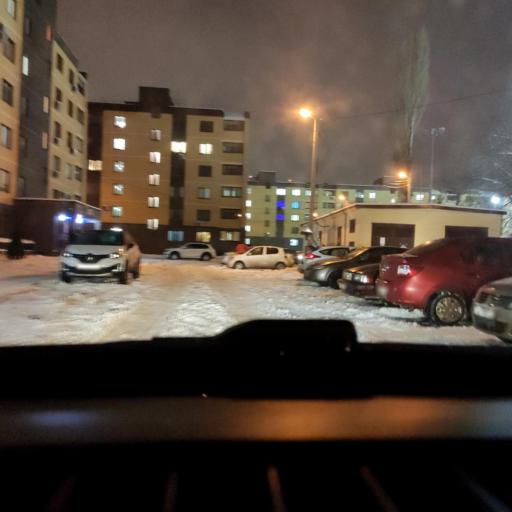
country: RU
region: Voronezj
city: Voronezh
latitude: 51.6672
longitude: 39.2795
